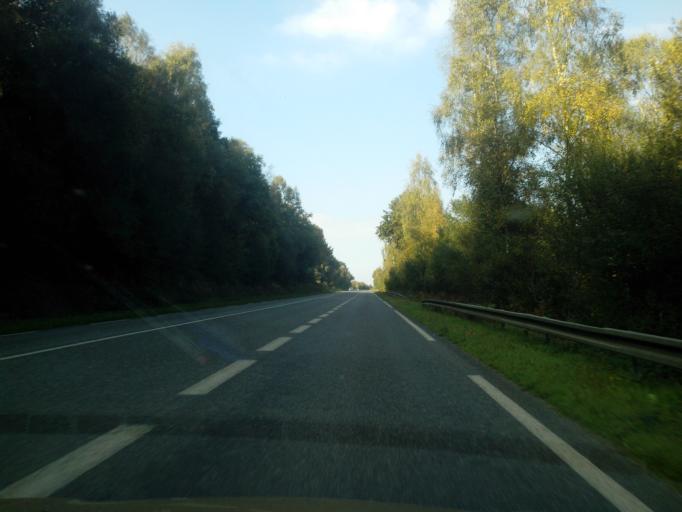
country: FR
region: Brittany
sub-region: Departement du Morbihan
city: Molac
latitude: 47.7237
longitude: -2.4399
